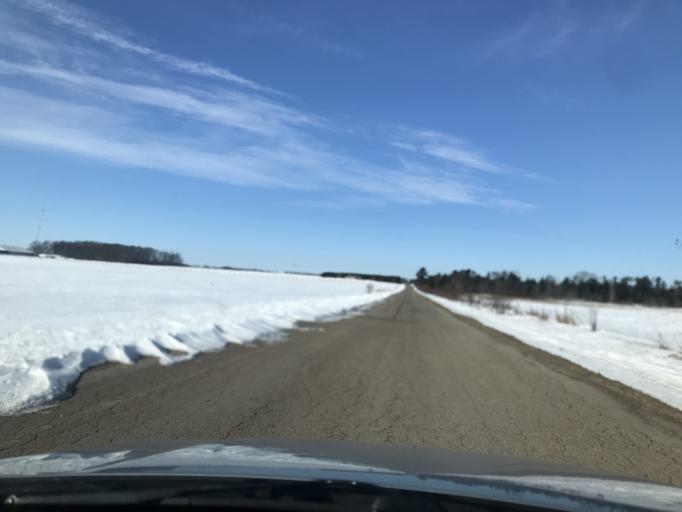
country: US
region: Wisconsin
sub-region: Oconto County
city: Oconto Falls
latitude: 44.9385
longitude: -88.2014
